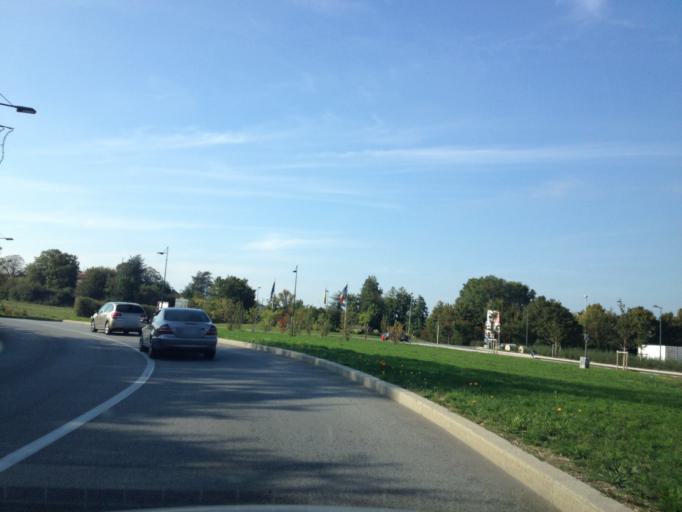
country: FR
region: Rhone-Alpes
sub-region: Departement de l'Isere
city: Villefontaine
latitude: 45.6118
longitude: 5.1539
